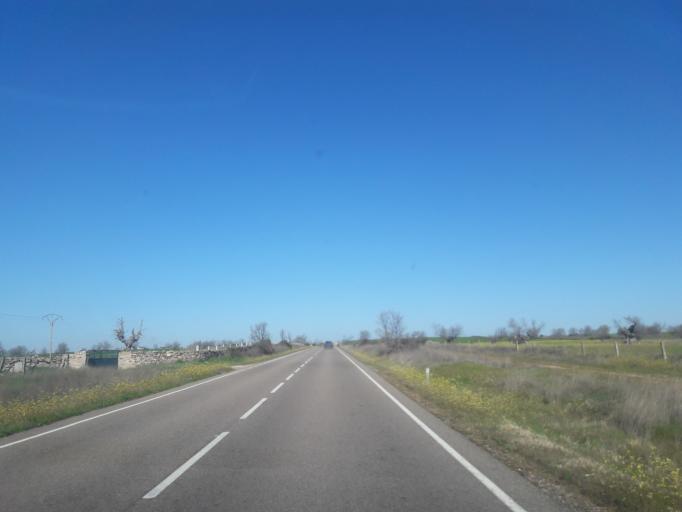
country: ES
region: Castille and Leon
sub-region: Provincia de Salamanca
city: Valderrodrigo
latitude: 41.0708
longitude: -6.5230
